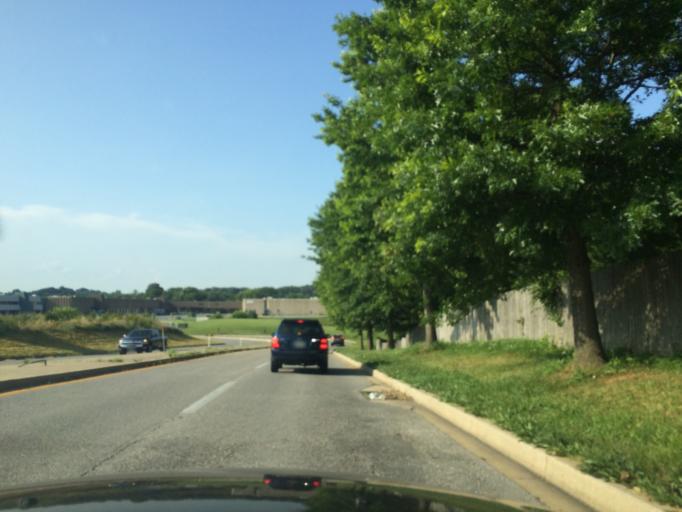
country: US
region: Maryland
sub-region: Carroll County
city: Eldersburg
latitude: 39.4048
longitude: -76.9438
